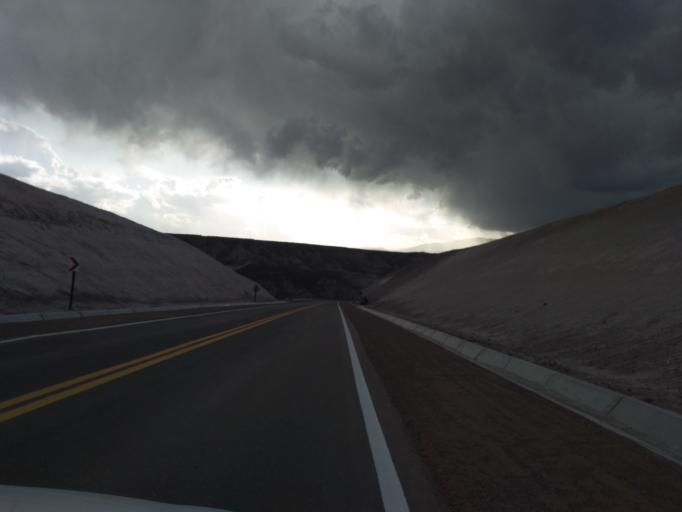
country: AR
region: Mendoza
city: La Consulta
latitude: -34.5525
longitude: -69.1699
